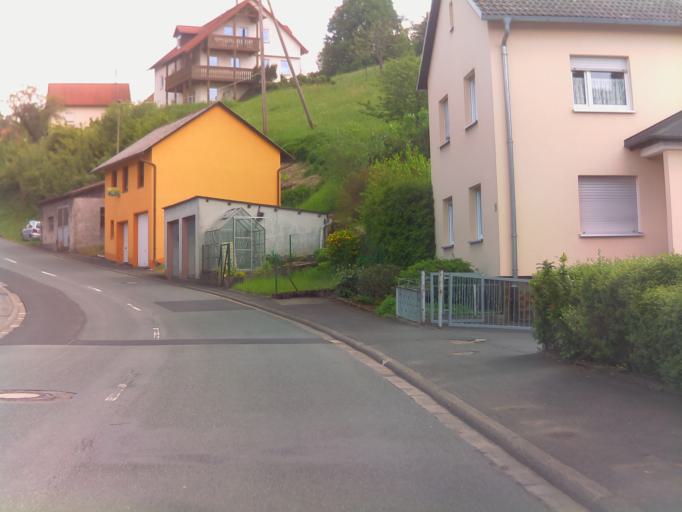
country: DE
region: Bavaria
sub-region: Regierungsbezirk Unterfranken
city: Sandberg
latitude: 50.3416
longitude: 10.0399
